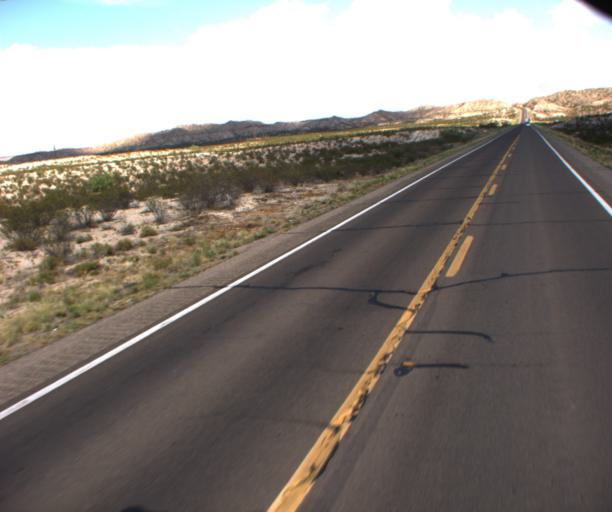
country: US
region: Arizona
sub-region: Greenlee County
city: Clifton
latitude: 32.7622
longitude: -109.1415
